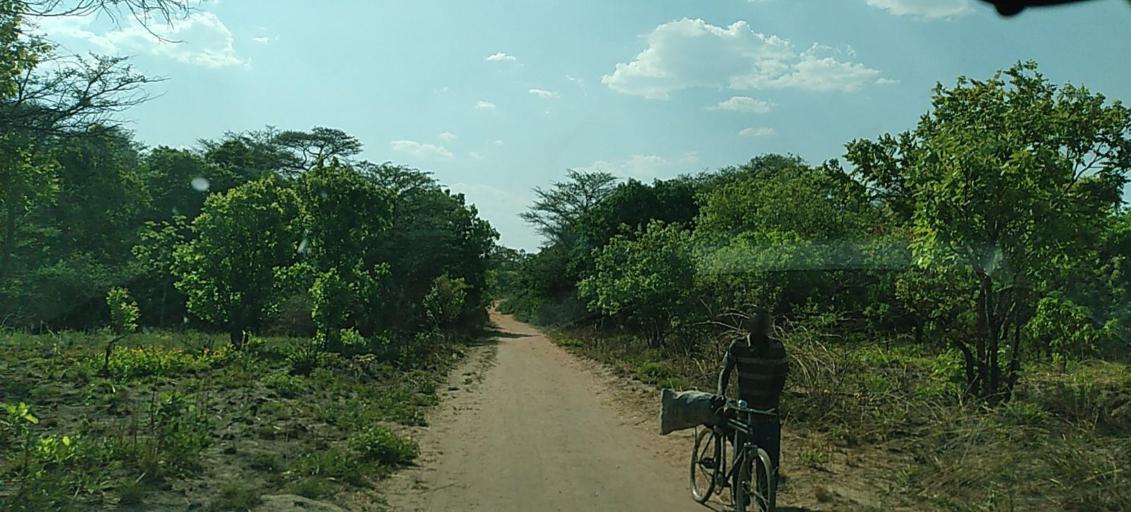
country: ZM
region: North-Western
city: Kalengwa
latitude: -13.1064
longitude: 24.9904
